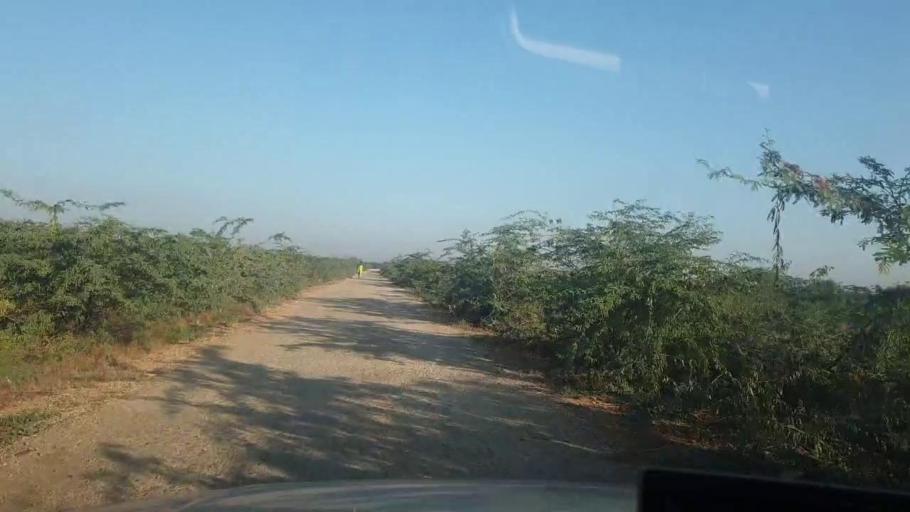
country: PK
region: Sindh
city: Thatta
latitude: 24.7084
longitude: 67.8472
